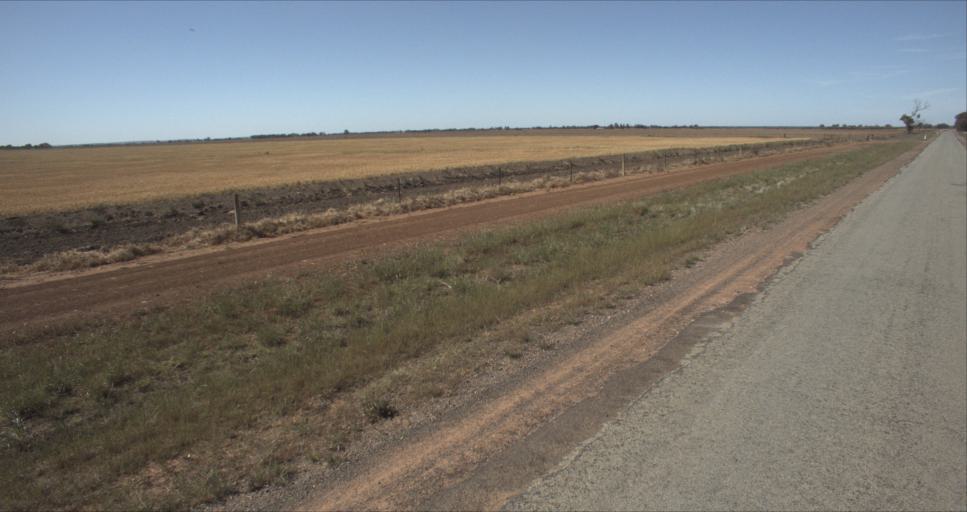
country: AU
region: New South Wales
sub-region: Leeton
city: Leeton
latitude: -34.5528
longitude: 146.3142
